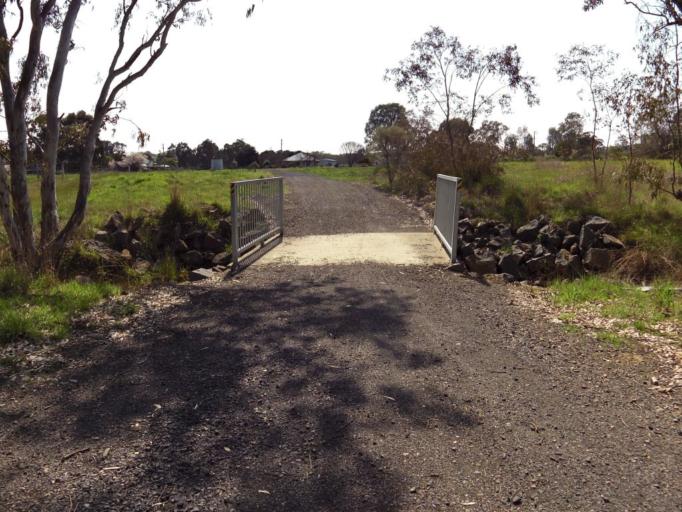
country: AU
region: Victoria
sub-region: Murrindindi
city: Alexandra
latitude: -37.1027
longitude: 145.6181
